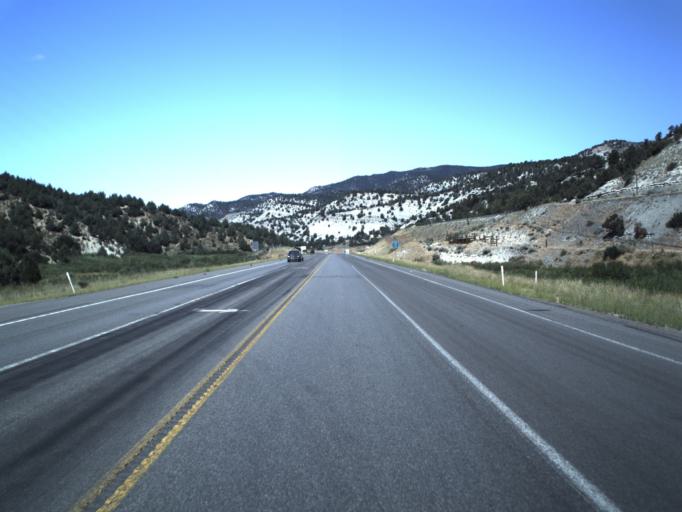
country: US
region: Utah
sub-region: Sanpete County
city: Fairview
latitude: 39.9503
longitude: -111.2196
